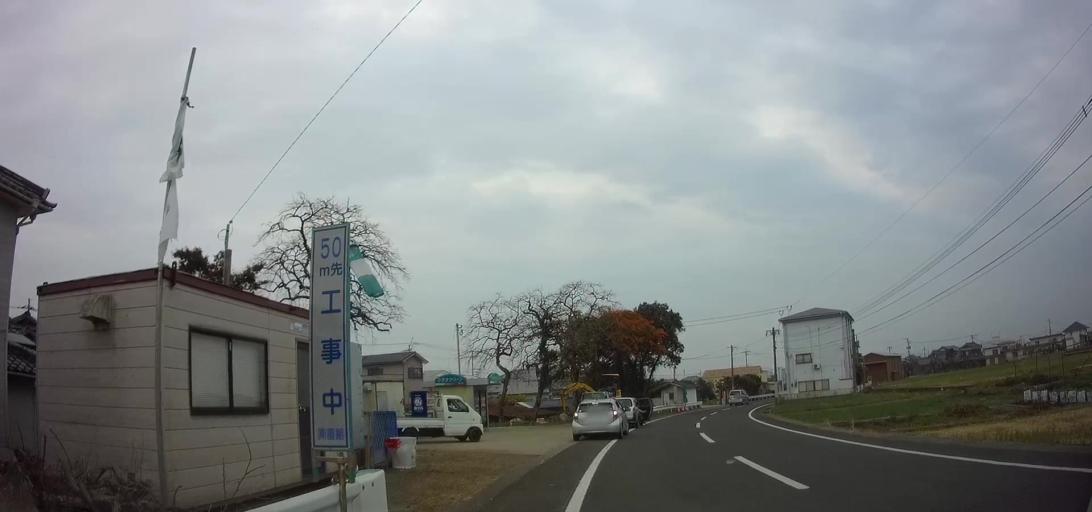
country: JP
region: Nagasaki
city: Shimabara
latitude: 32.6651
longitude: 130.3004
